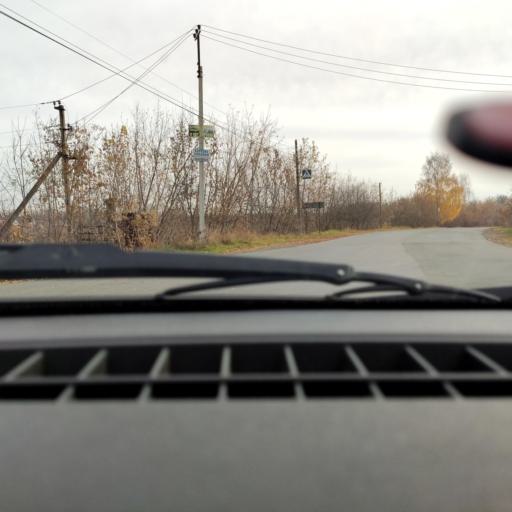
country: RU
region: Bashkortostan
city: Iglino
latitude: 54.8081
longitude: 56.1885
